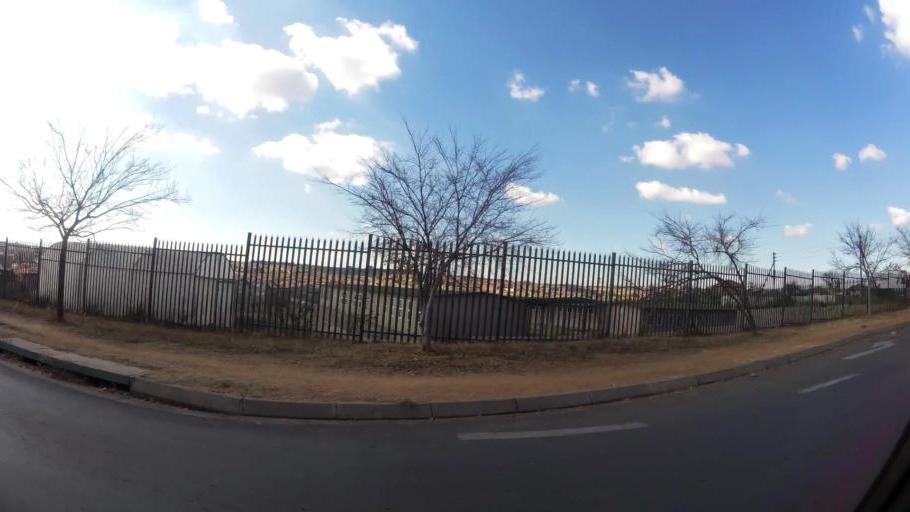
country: ZA
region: Gauteng
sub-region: West Rand District Municipality
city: Muldersdriseloop
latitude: -26.0405
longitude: 27.9143
